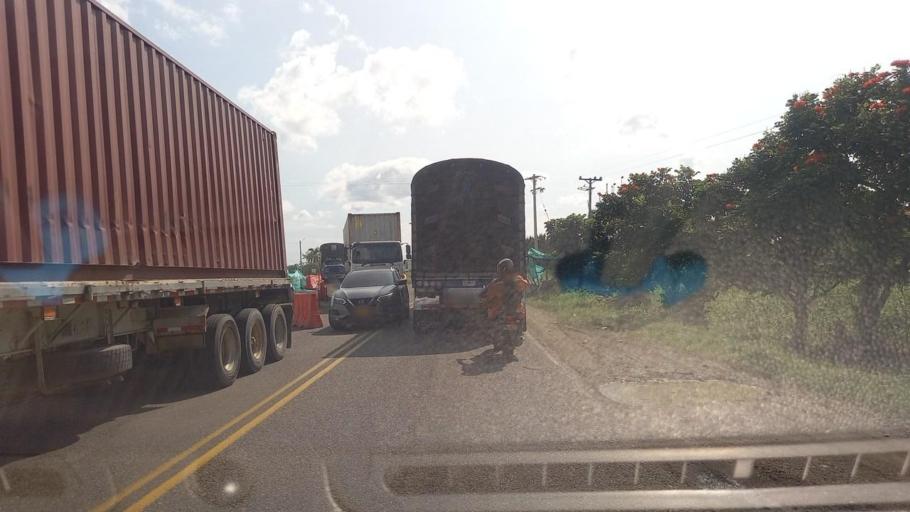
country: CO
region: Antioquia
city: Puerto Berrio
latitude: 6.2938
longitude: -74.4578
